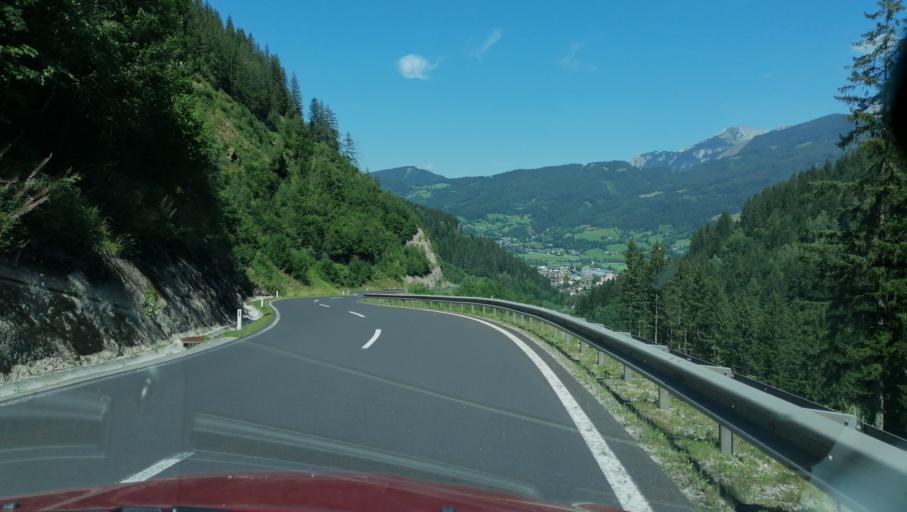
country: AT
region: Styria
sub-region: Politischer Bezirk Liezen
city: Trieben
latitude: 47.4707
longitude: 14.4853
